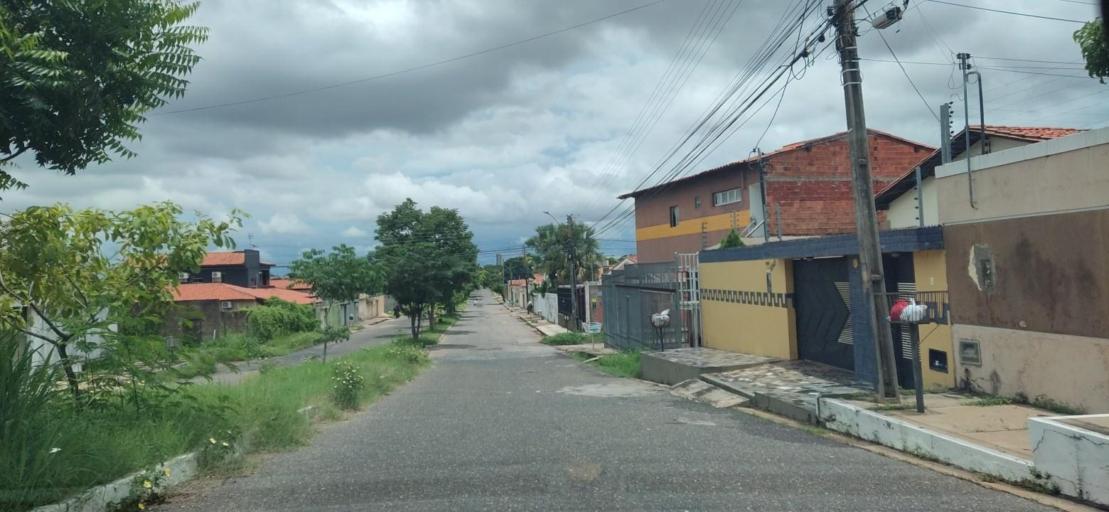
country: BR
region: Piaui
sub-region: Teresina
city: Teresina
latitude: -5.0745
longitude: -42.7529
